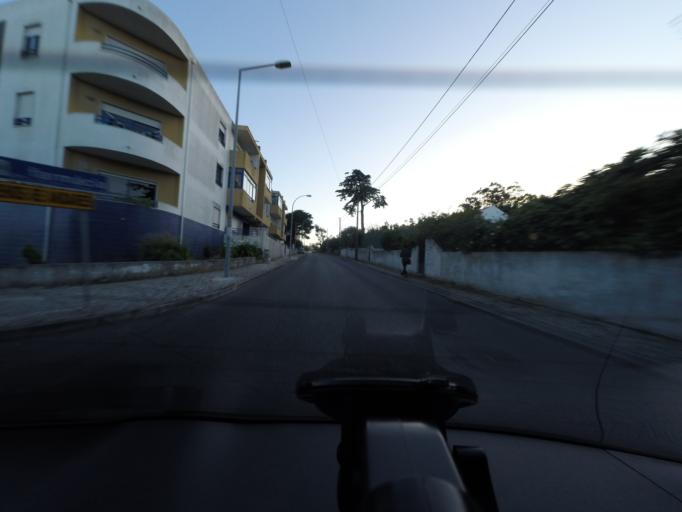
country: PT
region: Lisbon
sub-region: Sintra
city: Rio de Mouro
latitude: 38.7599
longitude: -9.3521
